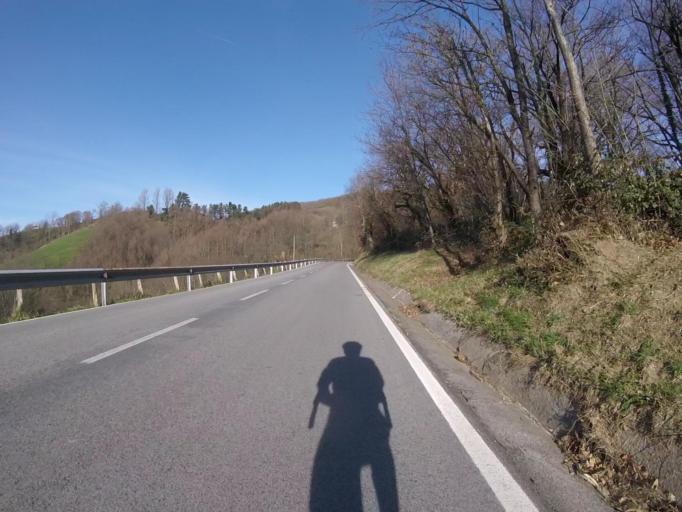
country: ES
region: Navarre
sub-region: Provincia de Navarra
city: Leitza
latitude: 43.0867
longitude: -1.9042
